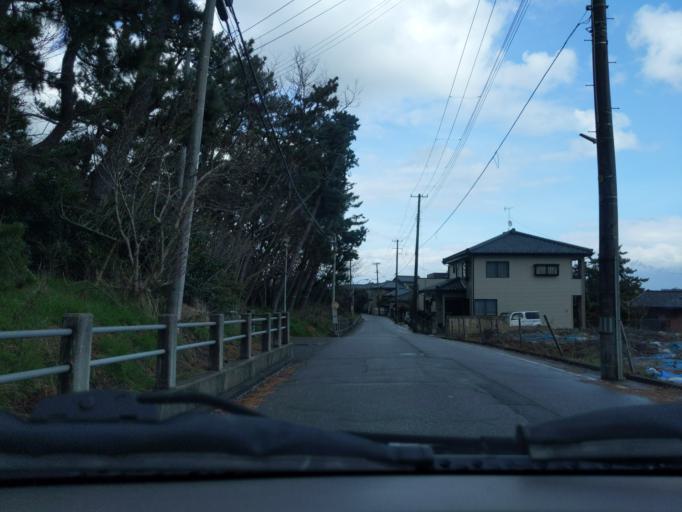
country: JP
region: Niigata
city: Niigata-shi
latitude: 37.9312
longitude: 139.0411
